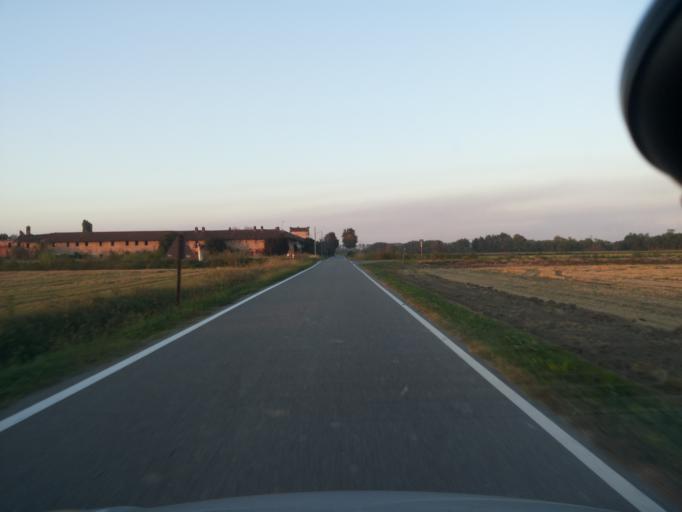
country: IT
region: Piedmont
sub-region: Provincia di Vercelli
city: San Germano Vercellese
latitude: 45.3904
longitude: 8.2401
